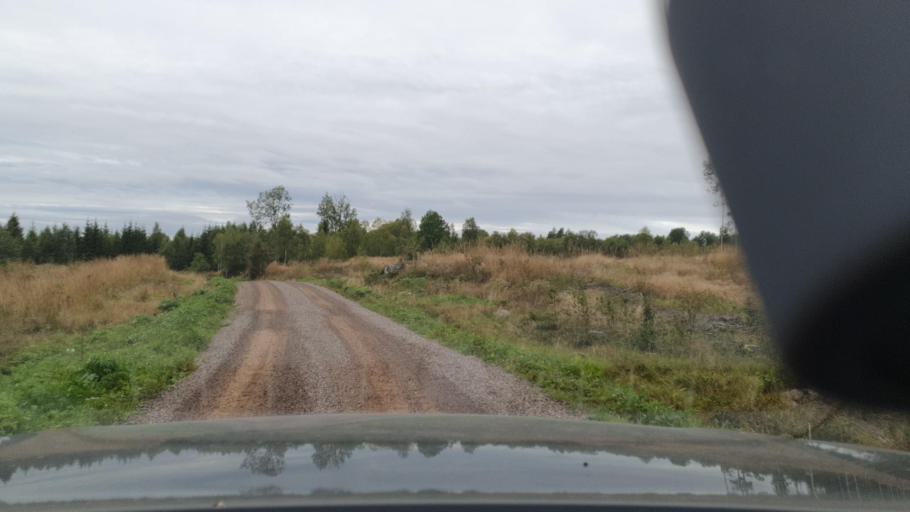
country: SE
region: Vaermland
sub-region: Torsby Kommun
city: Torsby
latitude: 59.9548
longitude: 12.7385
